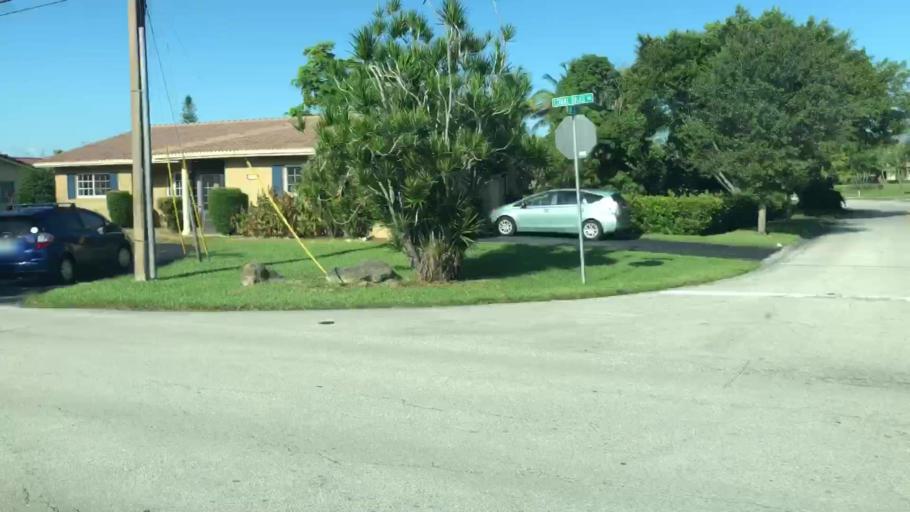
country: US
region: Florida
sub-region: Broward County
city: Coral Springs
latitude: 26.2789
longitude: -80.2565
